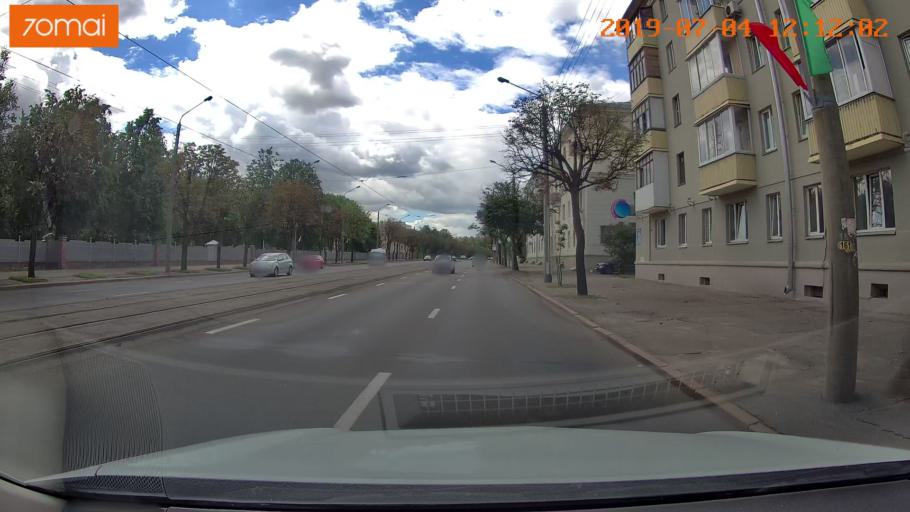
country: BY
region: Minsk
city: Minsk
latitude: 53.9343
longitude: 27.6021
